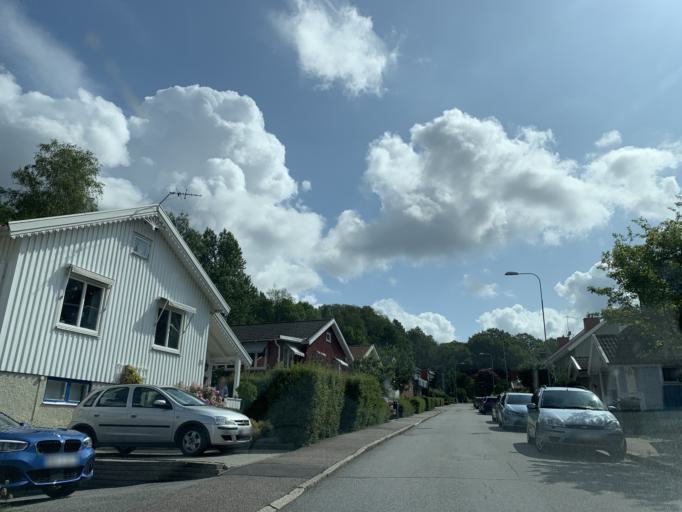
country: SE
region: Vaestra Goetaland
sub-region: Goteborg
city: Eriksbo
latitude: 57.7458
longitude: 12.0531
